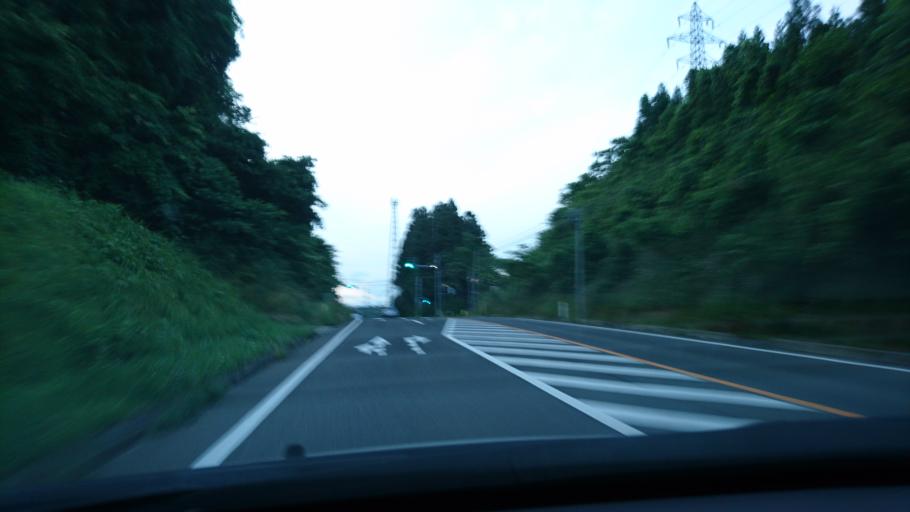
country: JP
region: Iwate
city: Ichinoseki
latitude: 38.7771
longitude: 140.9941
